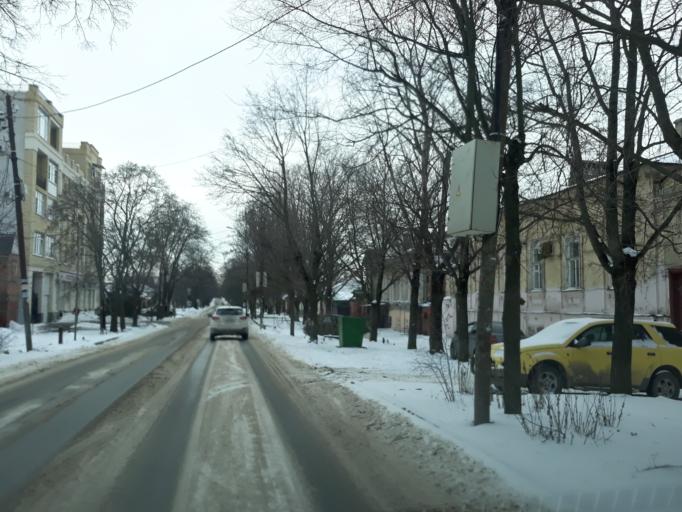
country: RU
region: Rostov
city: Taganrog
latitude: 47.2090
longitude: 38.9230
